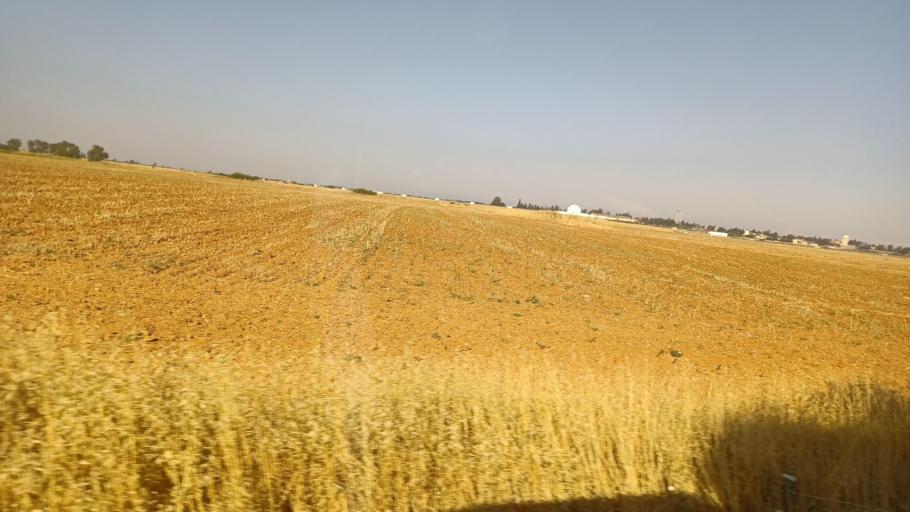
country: CY
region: Ammochostos
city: Frenaros
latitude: 35.0848
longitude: 33.9091
